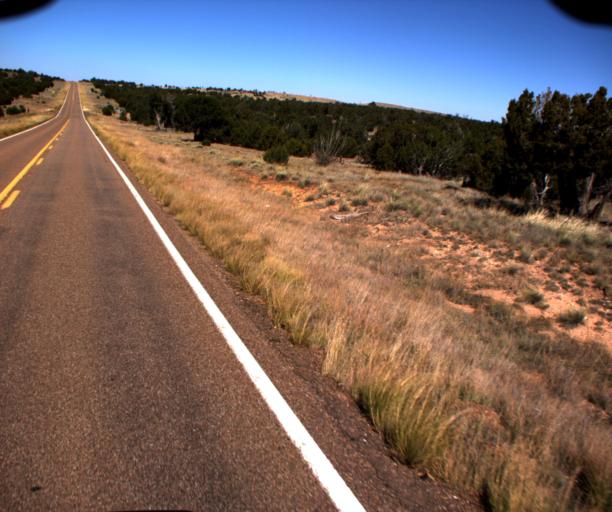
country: US
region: Arizona
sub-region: Navajo County
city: Heber-Overgaard
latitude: 34.4586
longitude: -110.4667
